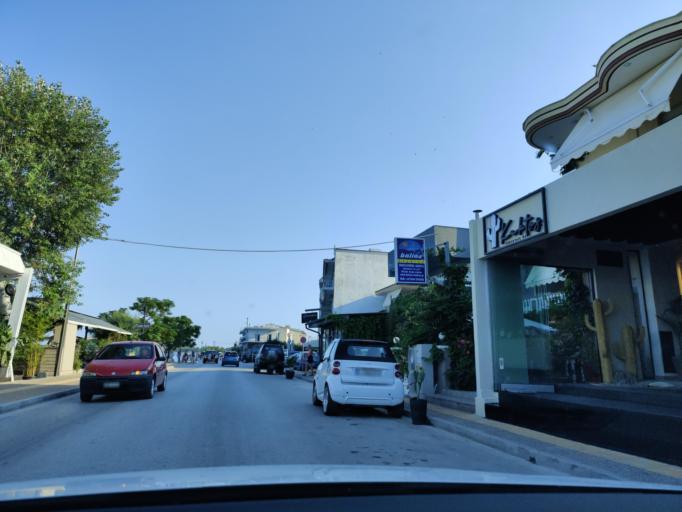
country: GR
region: East Macedonia and Thrace
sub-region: Nomos Kavalas
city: Nea Peramos
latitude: 40.8384
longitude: 24.3051
